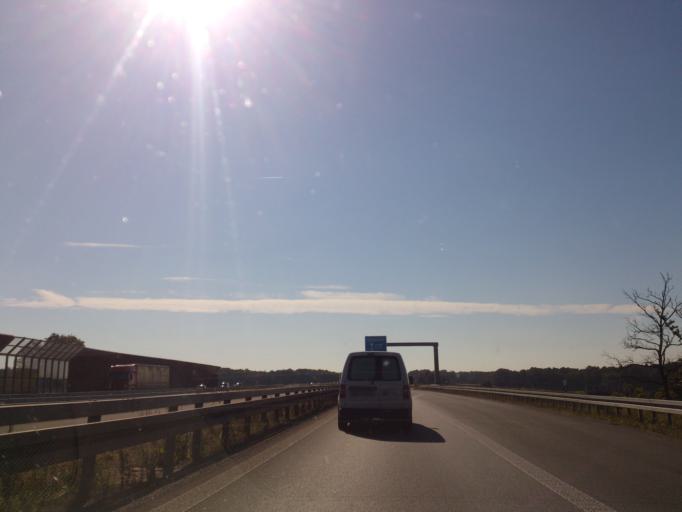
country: DE
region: North Rhine-Westphalia
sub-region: Regierungsbezirk Detmold
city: Bielefeld
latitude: 51.9767
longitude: 8.4822
